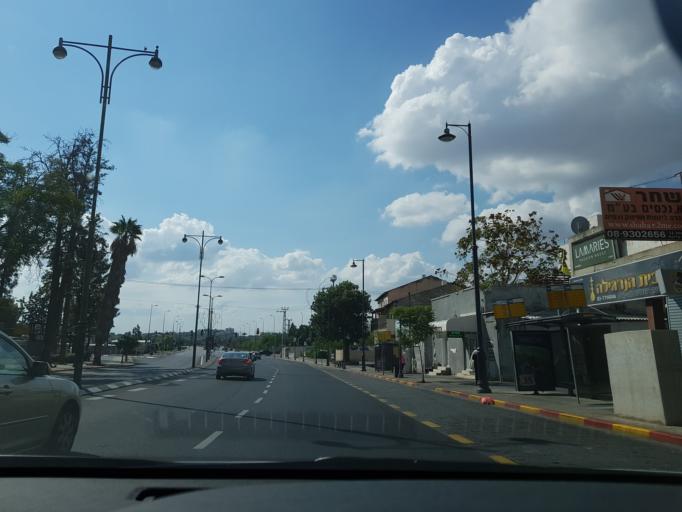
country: IL
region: Central District
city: Ness Ziona
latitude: 31.9258
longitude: 34.7978
